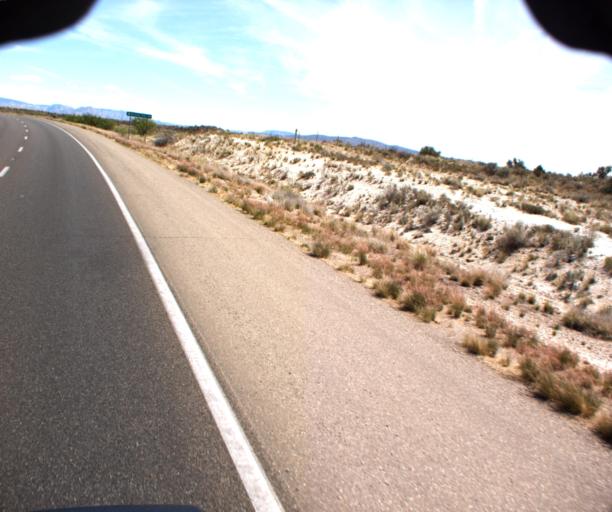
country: US
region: Arizona
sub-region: Yavapai County
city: Verde Village
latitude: 34.7233
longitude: -111.9850
